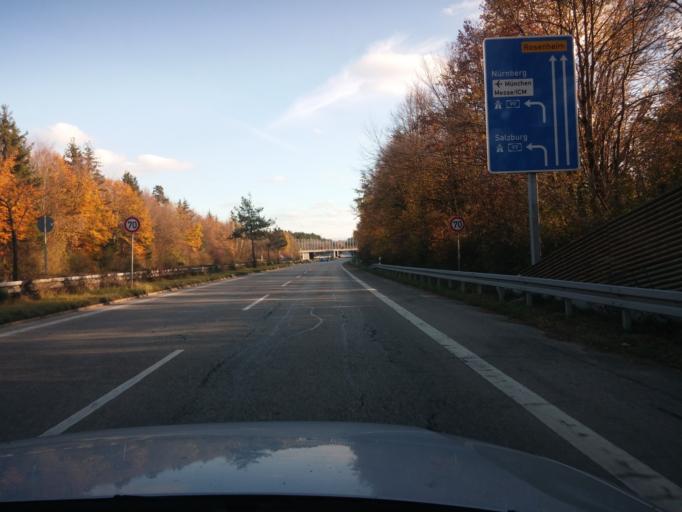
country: DE
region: Bavaria
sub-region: Upper Bavaria
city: Ottobrunn
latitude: 48.0425
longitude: 11.6764
